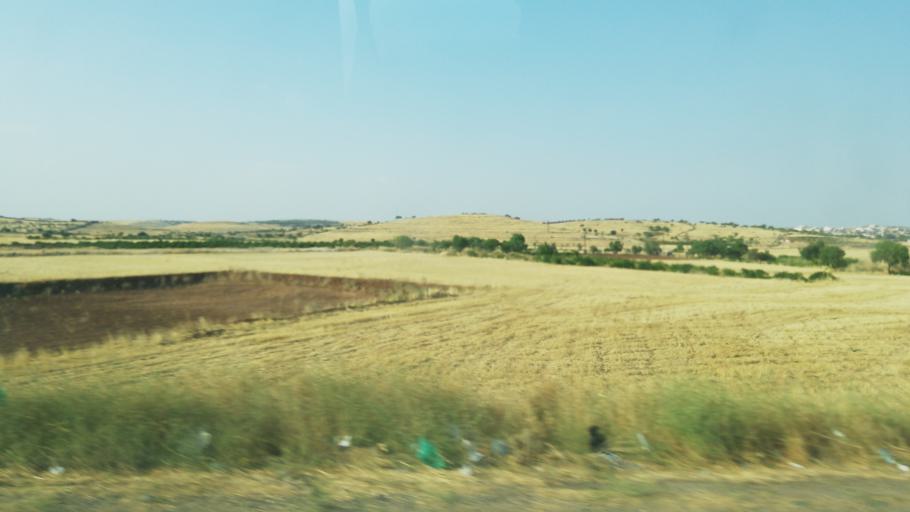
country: TR
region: Mardin
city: Acirli
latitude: 37.4478
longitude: 41.2757
